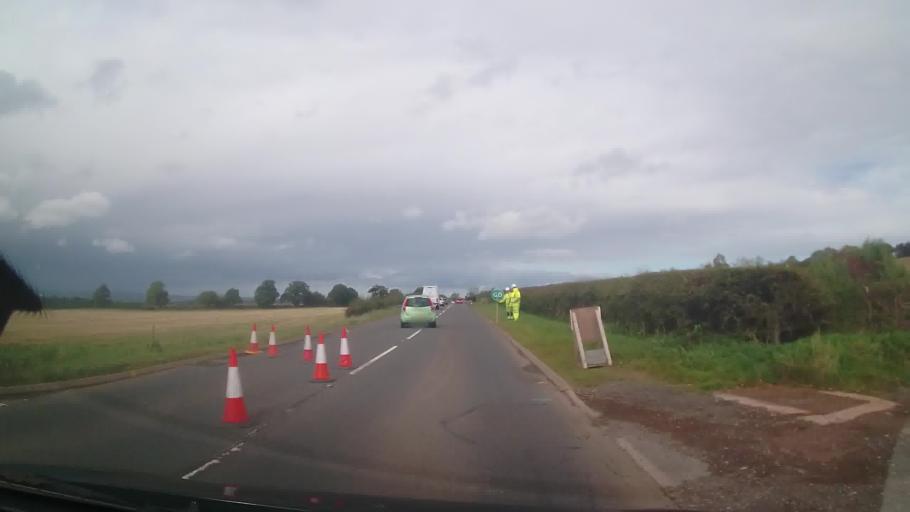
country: GB
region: England
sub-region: Shropshire
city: Alveley
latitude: 52.4793
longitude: -2.3539
